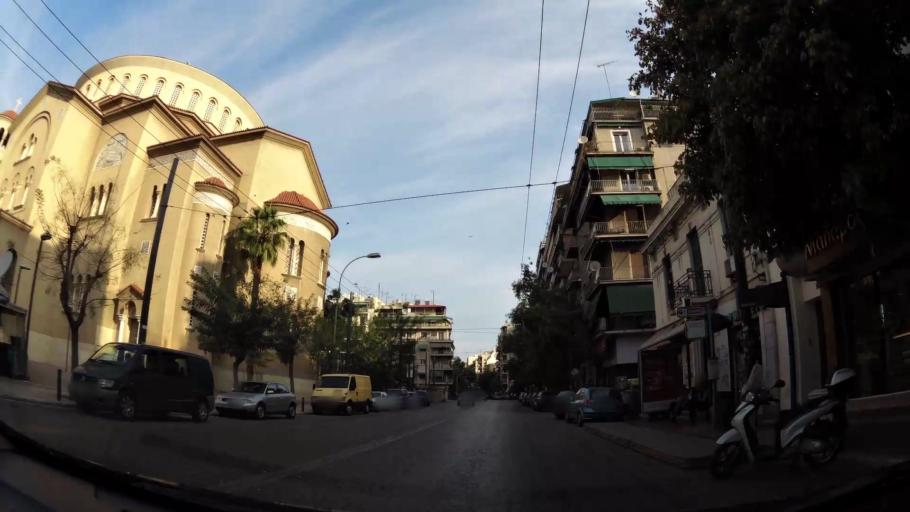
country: GR
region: Attica
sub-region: Nomarchia Athinas
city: Kipseli
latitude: 37.9966
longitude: 23.7273
